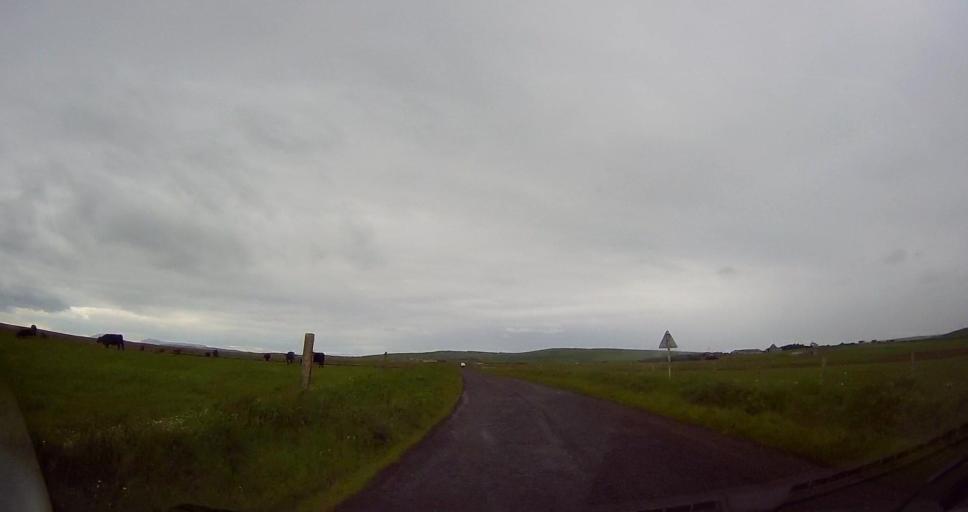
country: GB
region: Scotland
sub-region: Orkney Islands
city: Stromness
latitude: 59.1032
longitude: -3.2582
